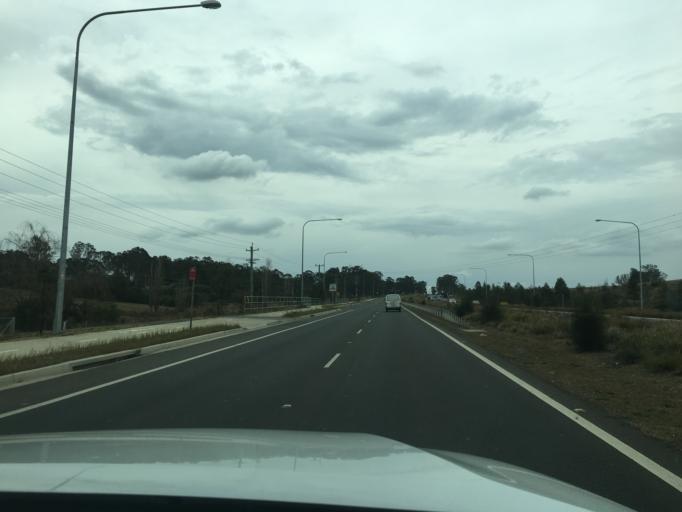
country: AU
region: New South Wales
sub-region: Campbelltown Municipality
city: Denham Court
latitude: -33.9912
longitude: 150.7896
